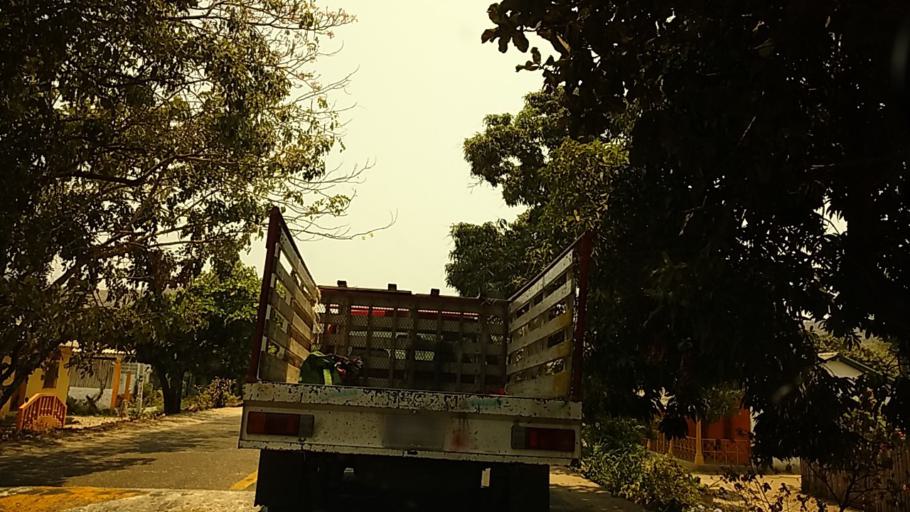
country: MX
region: Guerrero
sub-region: Atoyac de Alvarez
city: Zacualpan
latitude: 17.0370
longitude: -100.2514
